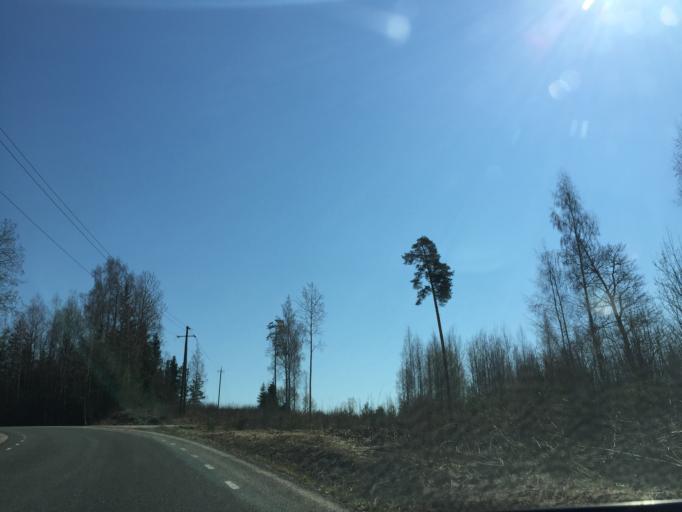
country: EE
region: Tartu
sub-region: Alatskivi vald
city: Kallaste
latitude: 58.5725
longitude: 26.9610
